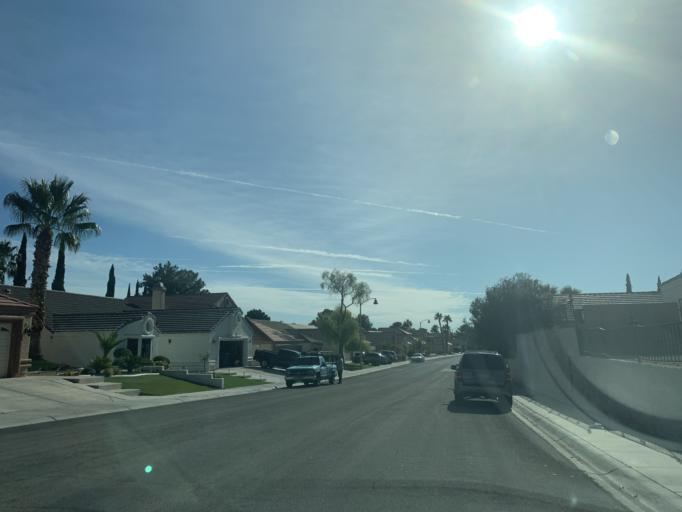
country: US
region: Nevada
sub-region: Clark County
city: Summerlin South
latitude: 36.1362
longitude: -115.2962
